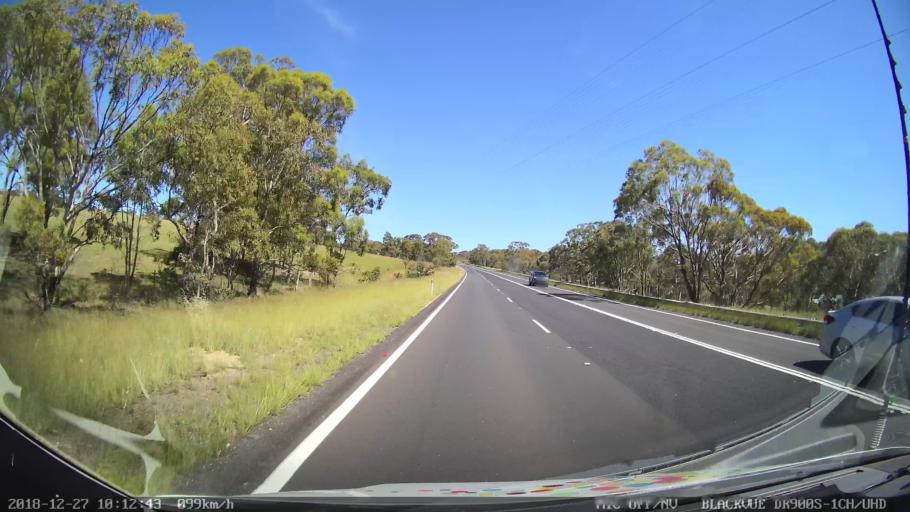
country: AU
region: New South Wales
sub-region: Bathurst Regional
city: Kelso
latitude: -33.4402
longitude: 149.7571
